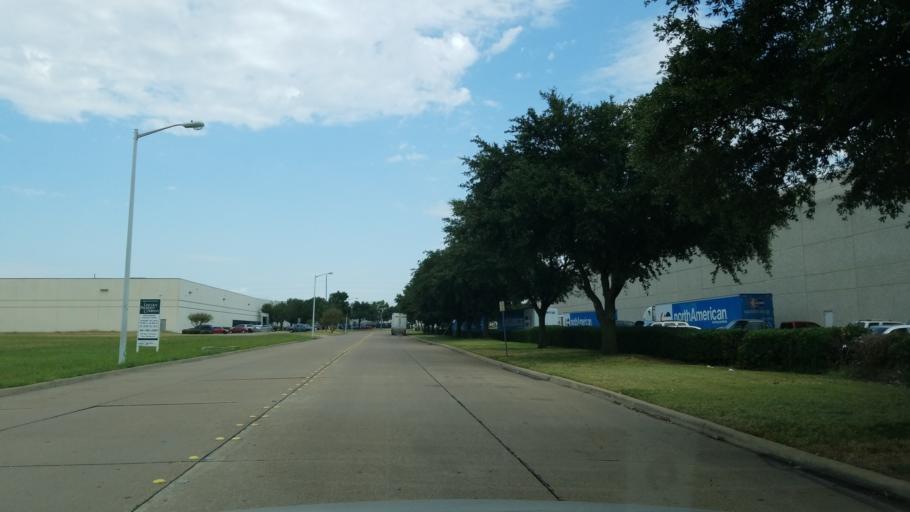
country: US
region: Texas
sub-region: Dallas County
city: Garland
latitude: 32.9041
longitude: -96.6741
